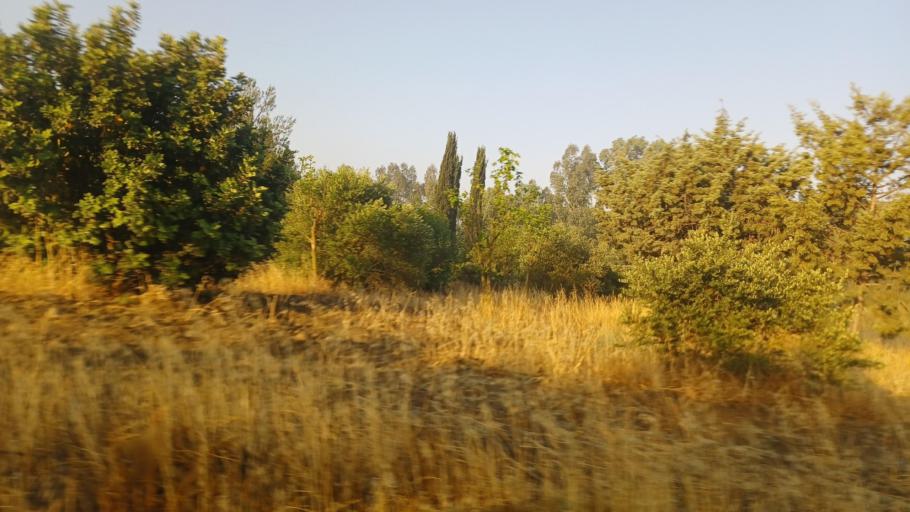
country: CY
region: Lefkosia
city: Alampra
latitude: 34.9771
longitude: 33.4188
